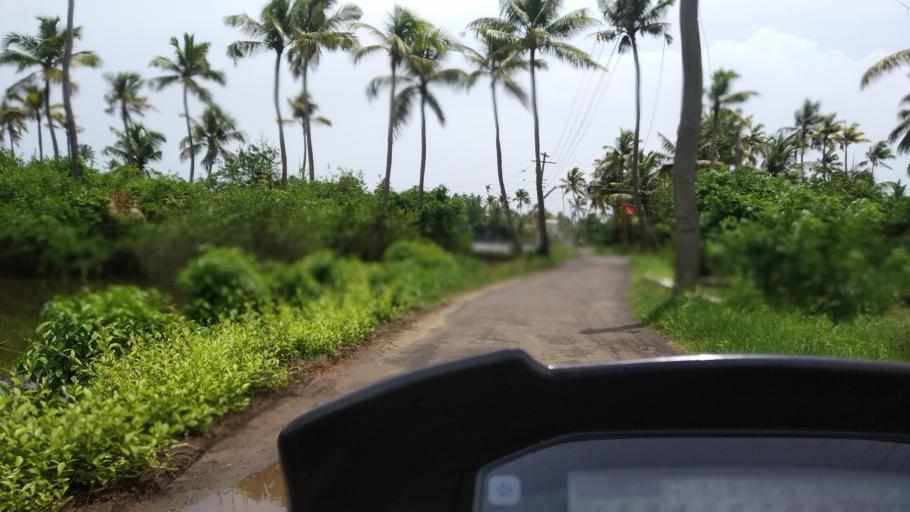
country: IN
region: Kerala
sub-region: Ernakulam
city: Elur
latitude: 10.0837
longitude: 76.2009
